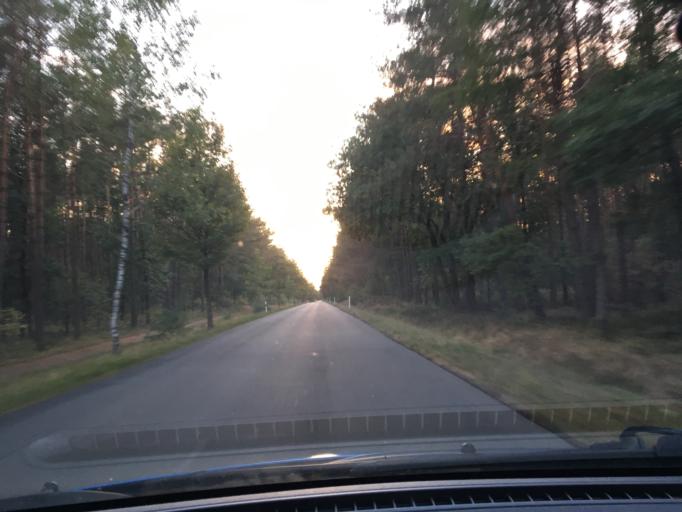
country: DE
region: Lower Saxony
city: Fassberg
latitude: 52.8953
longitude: 10.1494
